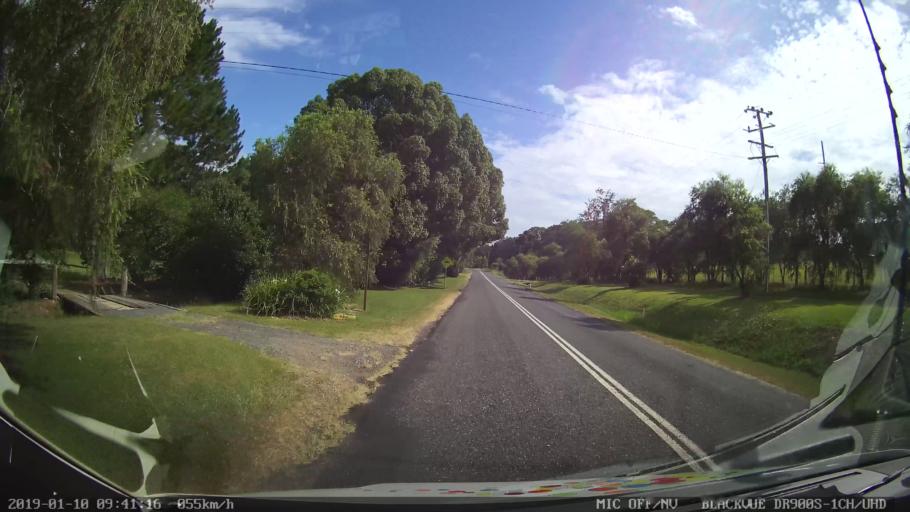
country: AU
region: New South Wales
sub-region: Coffs Harbour
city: Nana Glen
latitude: -30.1436
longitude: 153.0077
